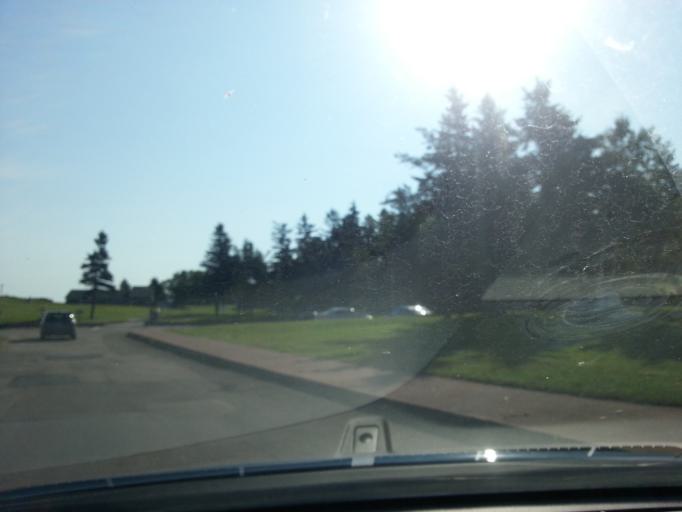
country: CA
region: New Brunswick
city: Shediac
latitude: 46.2386
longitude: -64.5077
